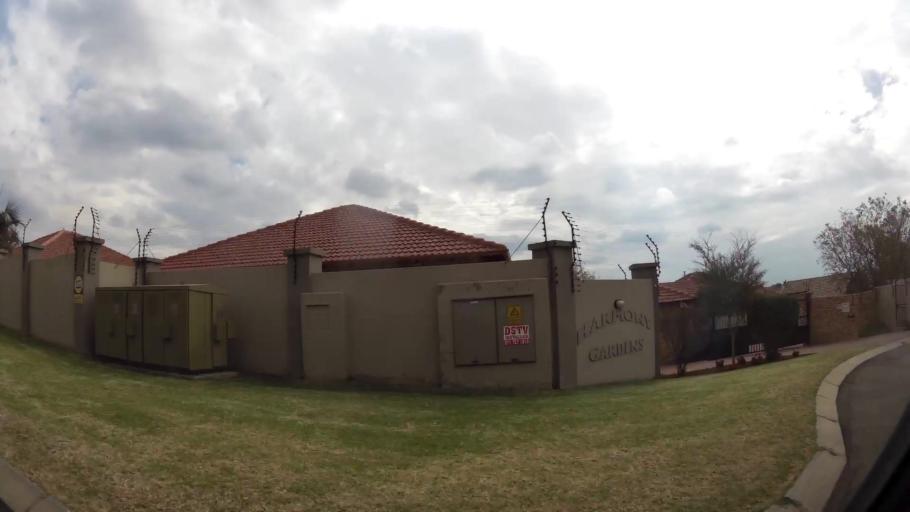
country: ZA
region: Gauteng
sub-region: City of Johannesburg Metropolitan Municipality
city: Roodepoort
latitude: -26.0991
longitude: 27.8797
